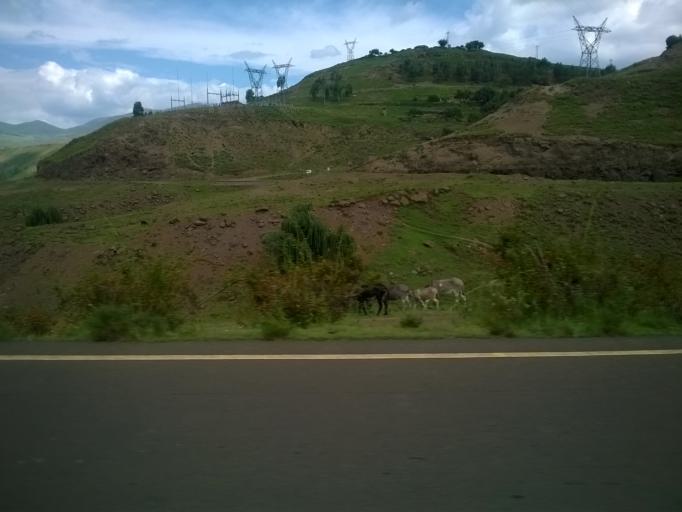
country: LS
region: Thaba-Tseka
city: Thaba-Tseka
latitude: -29.1633
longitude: 28.4782
